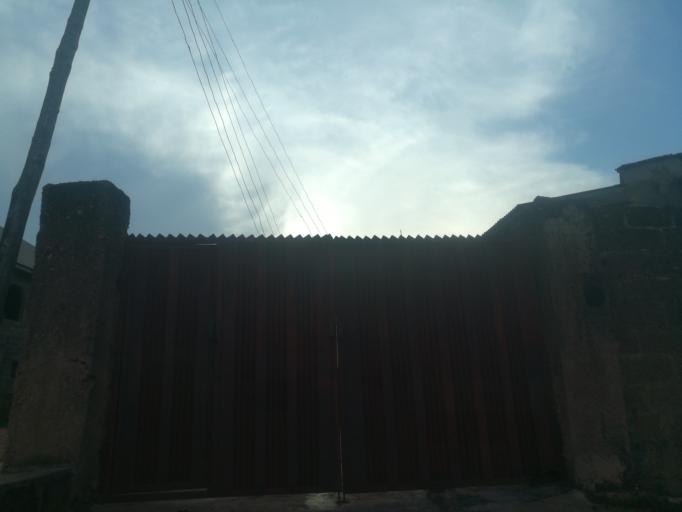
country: NG
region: Oyo
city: Moniya
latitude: 7.5277
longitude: 3.9089
